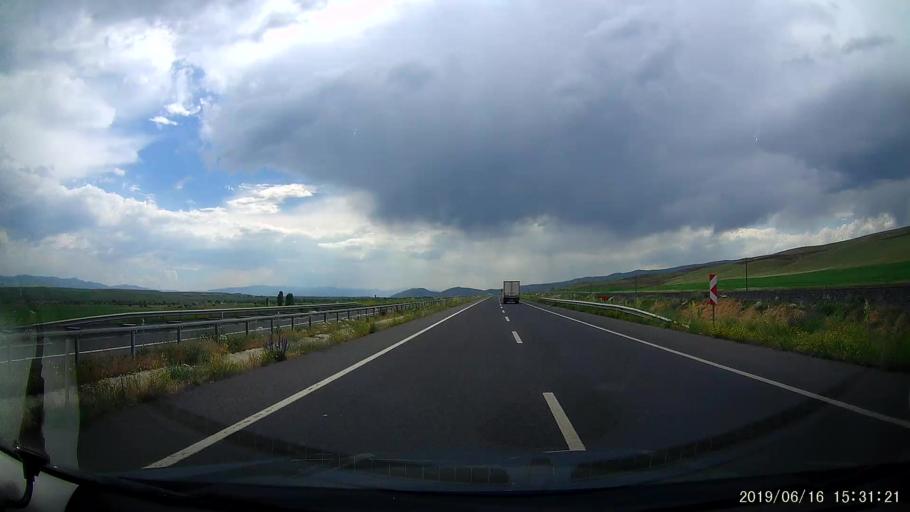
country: TR
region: Erzurum
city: Horasan
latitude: 40.0326
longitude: 42.0788
